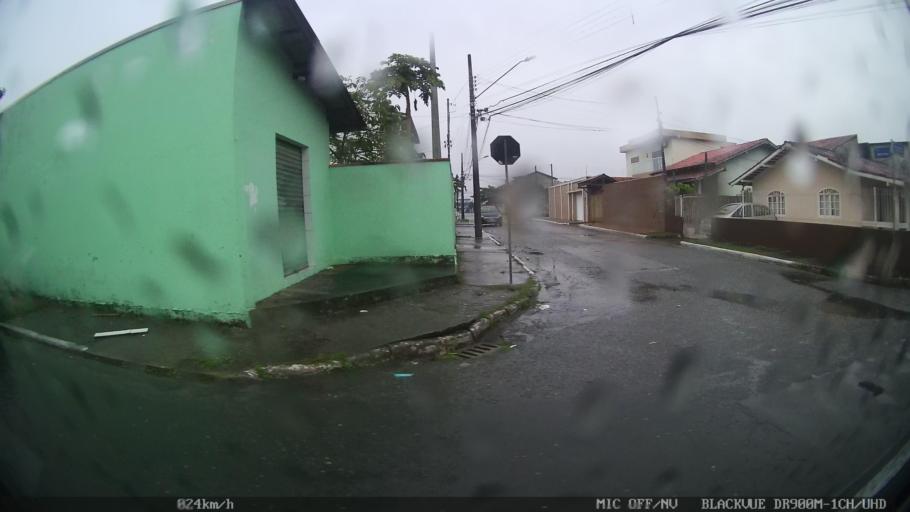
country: BR
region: Santa Catarina
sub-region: Itajai
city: Itajai
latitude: -26.9261
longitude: -48.6932
